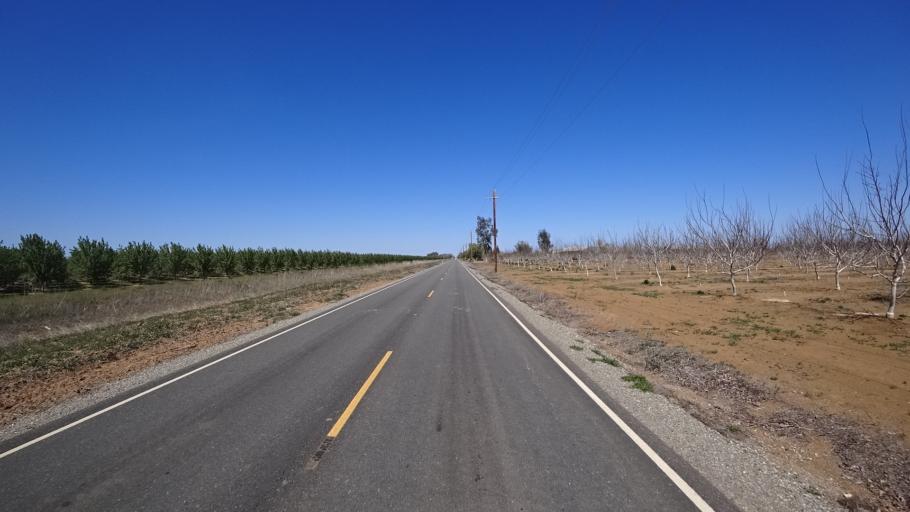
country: US
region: California
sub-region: Glenn County
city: Willows
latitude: 39.4975
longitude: -122.2491
